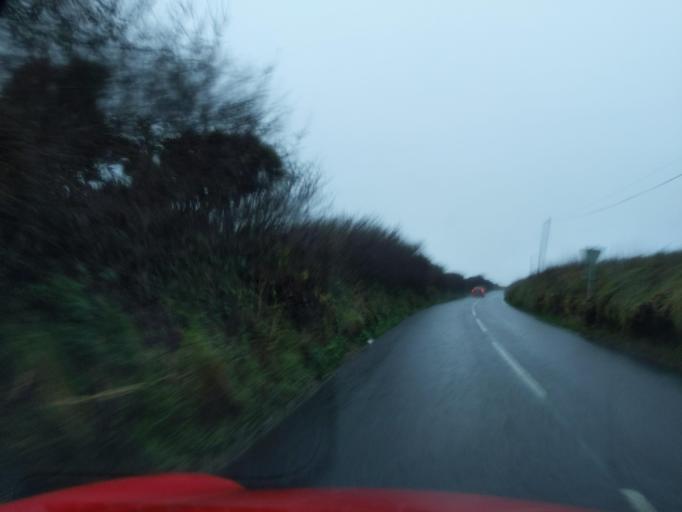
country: GB
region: England
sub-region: Cornwall
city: Camelford
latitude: 50.6396
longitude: -4.6933
